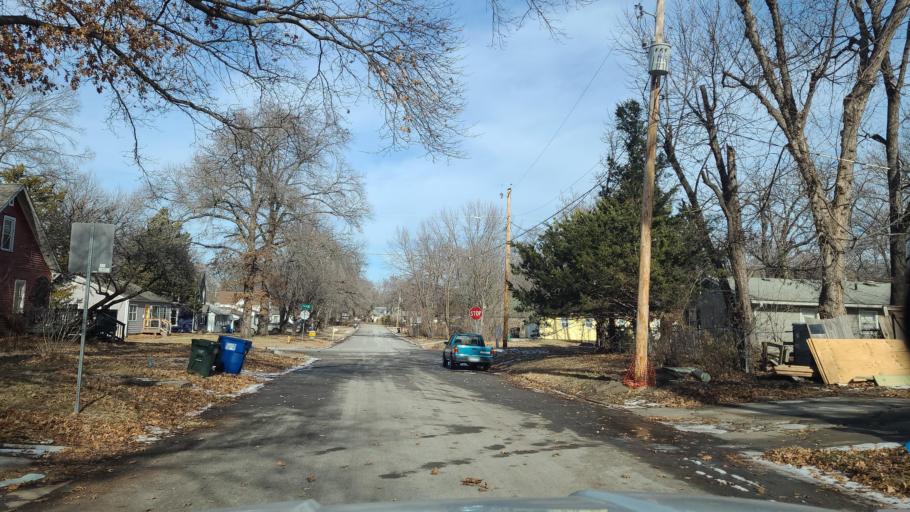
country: US
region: Kansas
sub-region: Douglas County
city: Lawrence
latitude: 38.9460
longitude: -95.2336
